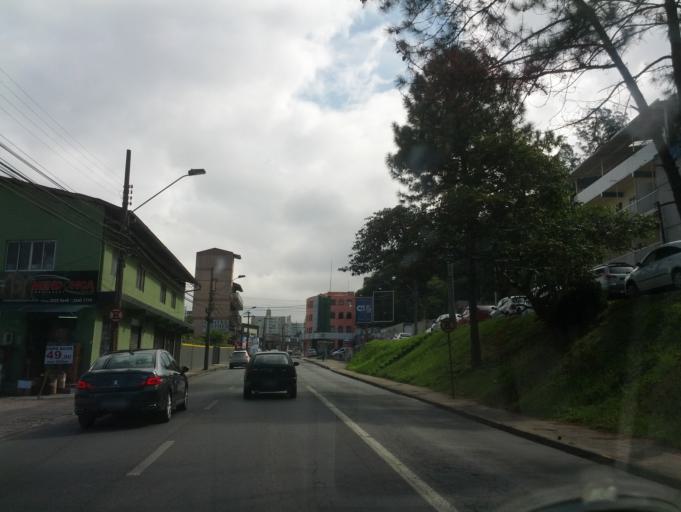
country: BR
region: Santa Catarina
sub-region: Blumenau
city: Blumenau
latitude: -26.9115
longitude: -49.0706
